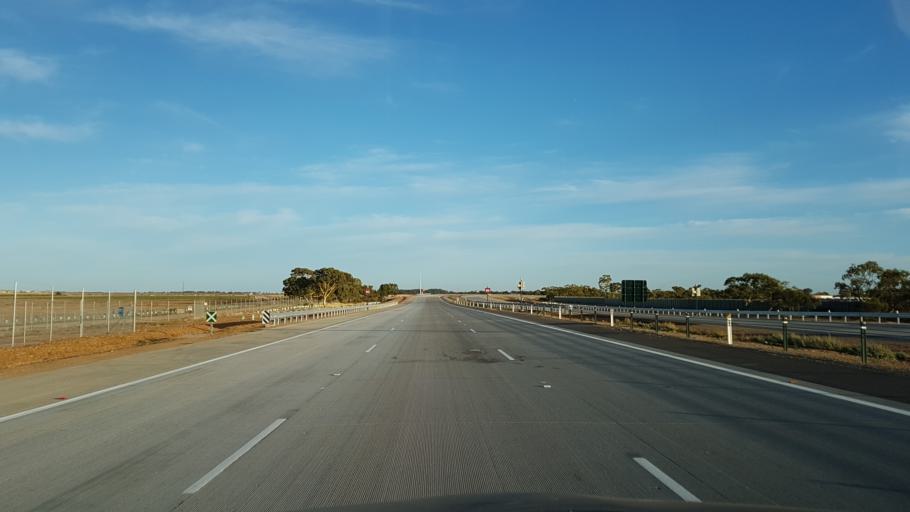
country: AU
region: South Australia
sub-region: Salisbury
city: Salisbury
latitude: -34.7549
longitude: 138.5856
